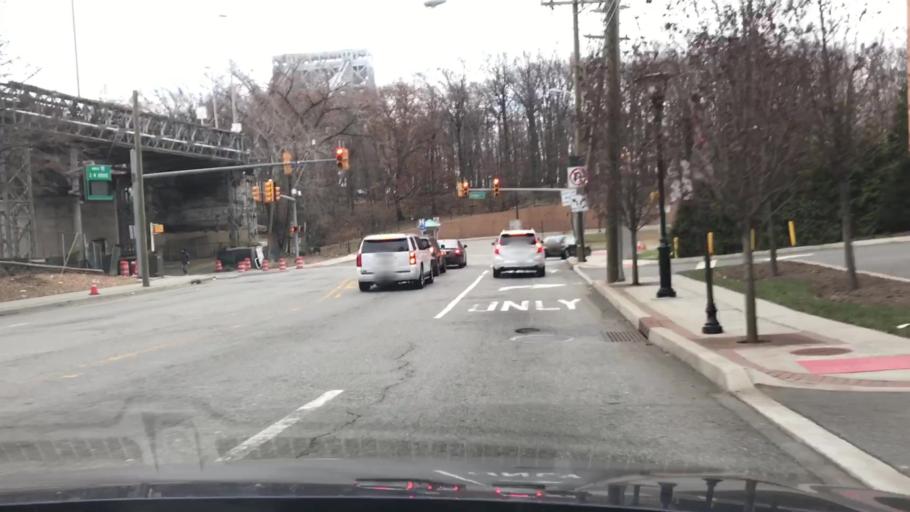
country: US
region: New Jersey
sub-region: Bergen County
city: Fort Lee
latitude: 40.8526
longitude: -73.9649
